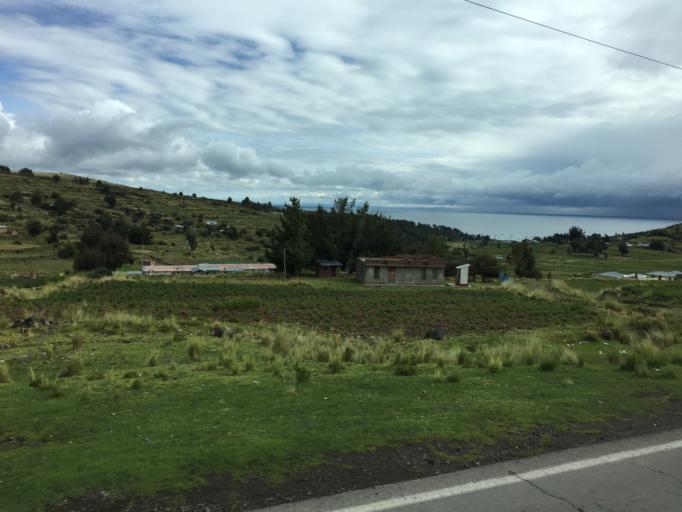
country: PE
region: Puno
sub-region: Provincia de Chucuito
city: Juli
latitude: -16.2025
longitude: -69.4213
